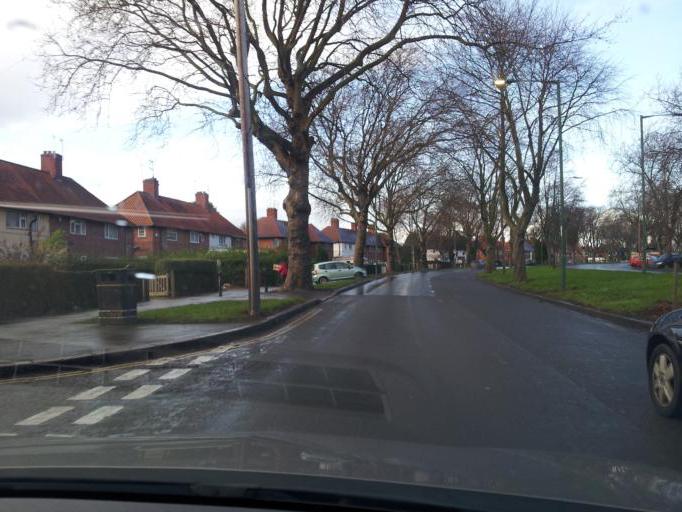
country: GB
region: England
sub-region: Nottingham
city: Nottingham
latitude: 52.9363
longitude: -1.2140
